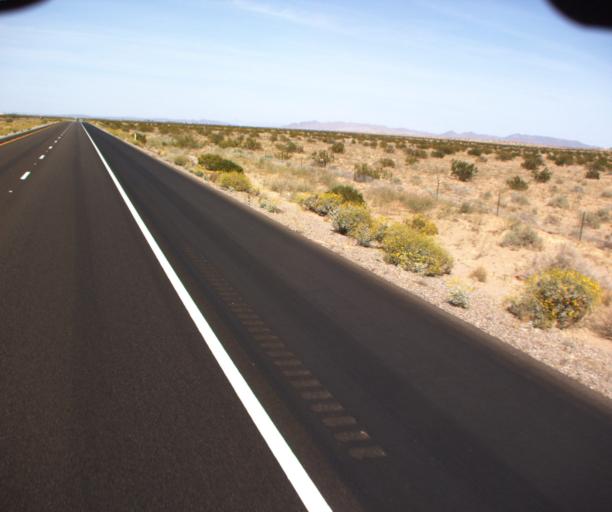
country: US
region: Arizona
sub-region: Yuma County
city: Somerton
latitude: 32.5803
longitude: -114.5525
